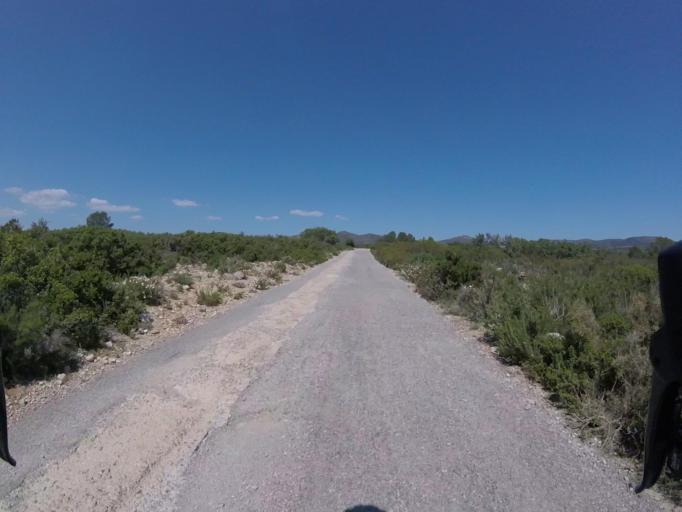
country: ES
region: Valencia
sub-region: Provincia de Castello
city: Sierra-Engarceran
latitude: 40.2240
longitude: -0.0214
